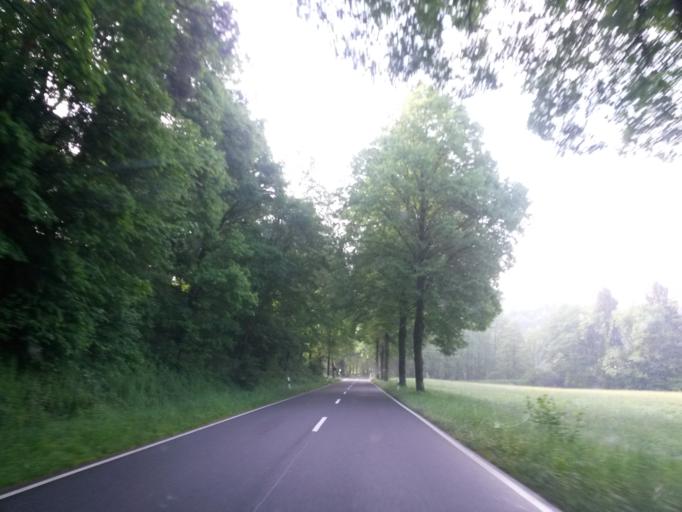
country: DE
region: North Rhine-Westphalia
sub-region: Regierungsbezirk Koln
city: Much
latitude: 50.8770
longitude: 7.3522
